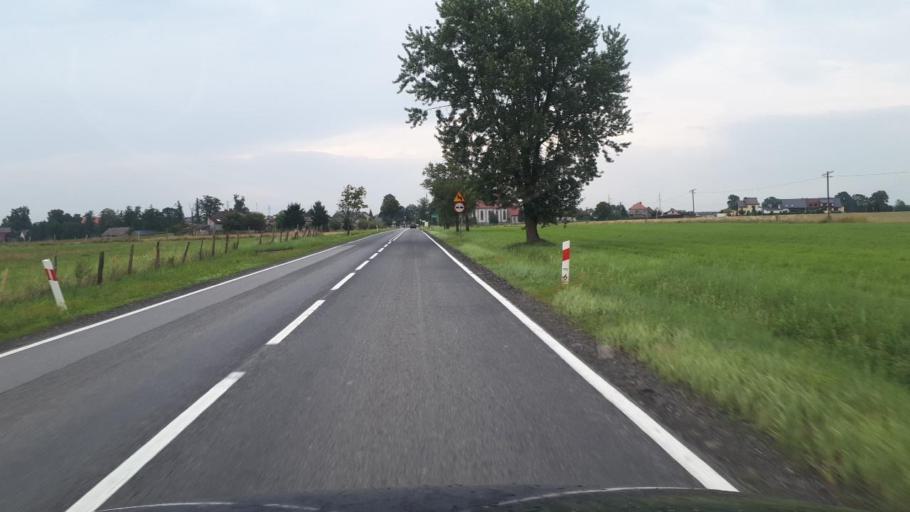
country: PL
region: Opole Voivodeship
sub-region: Powiat oleski
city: Olesno
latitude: 50.8449
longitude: 18.4880
